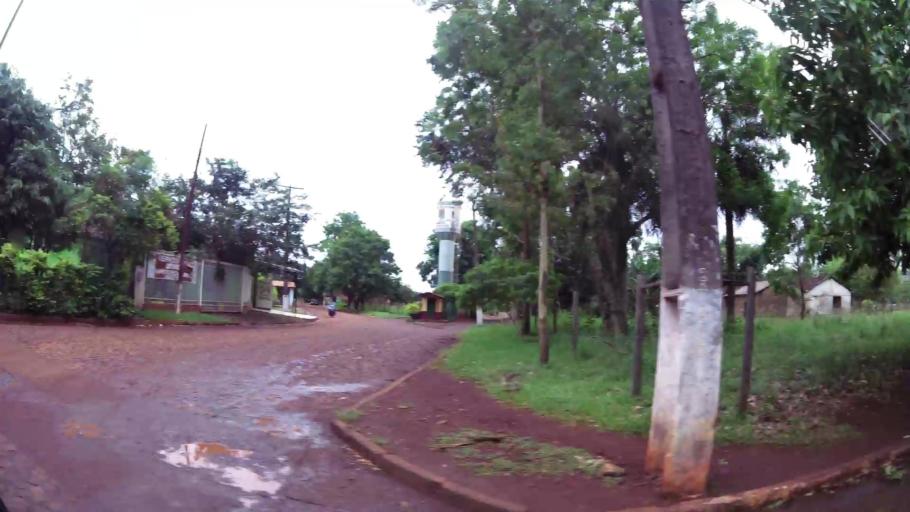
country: PY
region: Alto Parana
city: Presidente Franco
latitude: -25.4852
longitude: -54.7966
